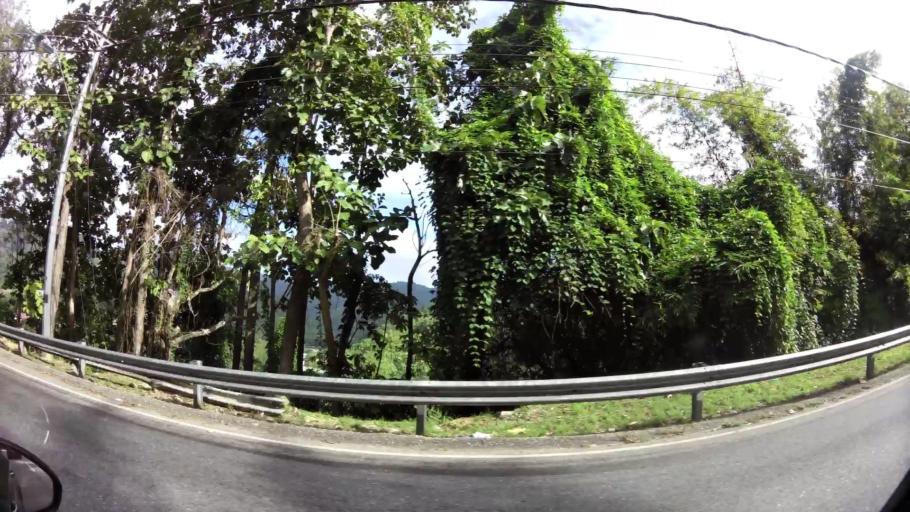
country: TT
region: Diego Martin
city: Petit Valley
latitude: 10.7138
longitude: -61.4992
